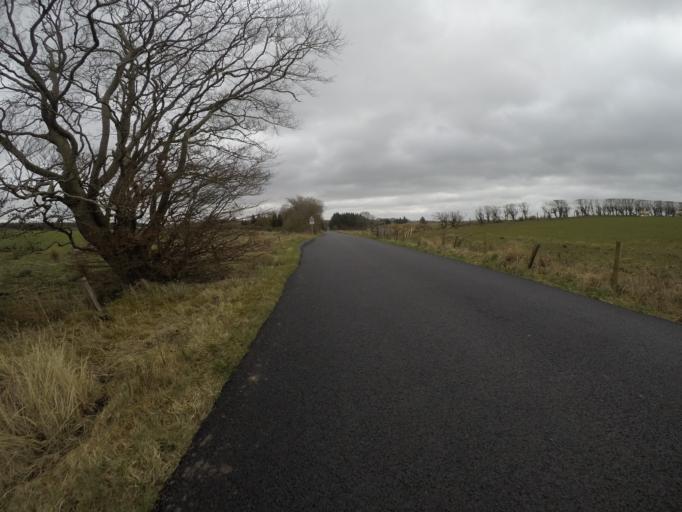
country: GB
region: Scotland
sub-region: East Ayrshire
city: Stewarton
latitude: 55.6810
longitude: -4.4573
